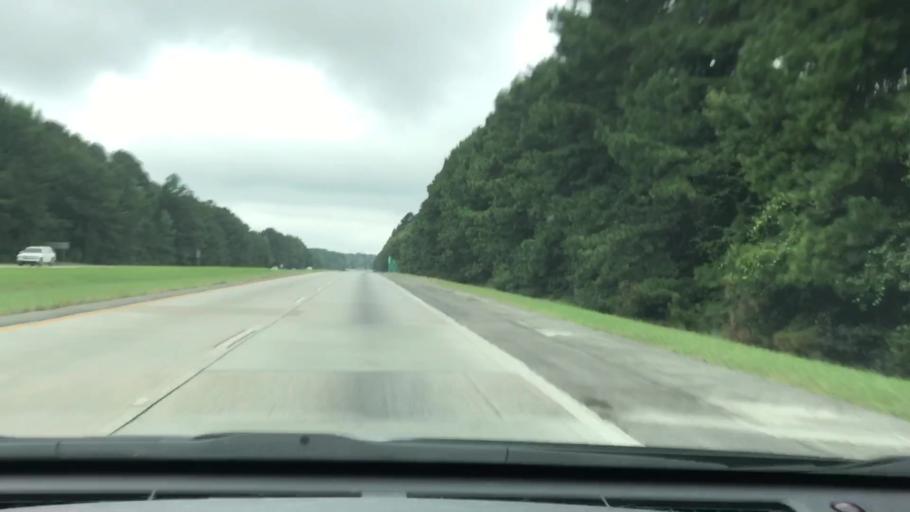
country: US
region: Georgia
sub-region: Greene County
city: Union Point
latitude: 33.5488
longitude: -83.0640
